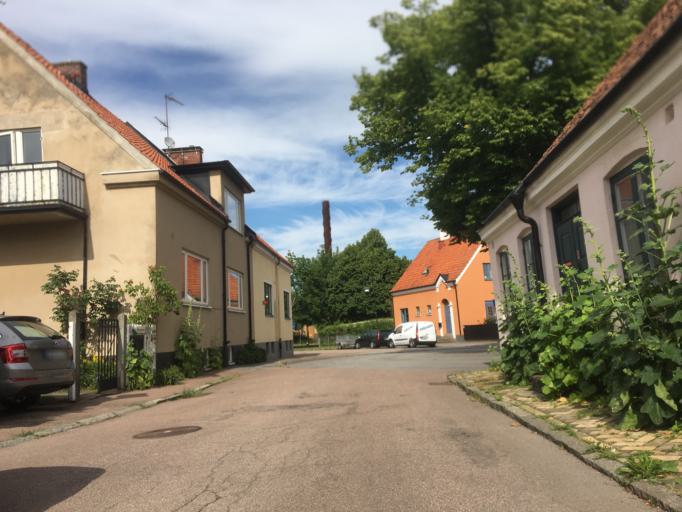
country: SE
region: Skane
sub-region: Landskrona
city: Landskrona
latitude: 55.8786
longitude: 12.8368
